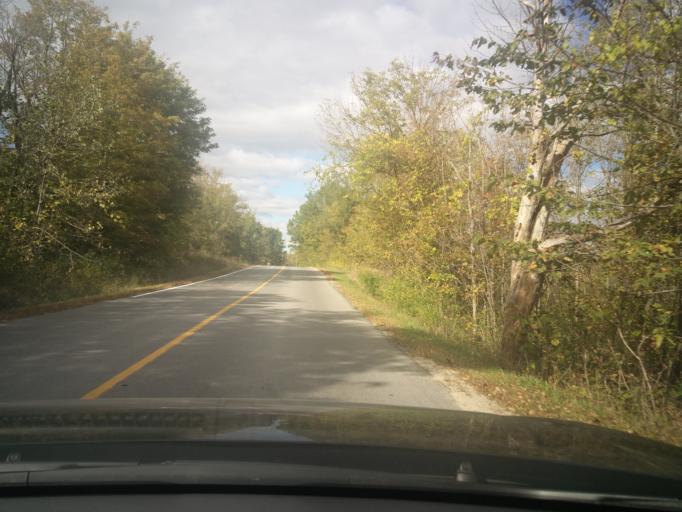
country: CA
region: Ontario
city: Perth
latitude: 44.6495
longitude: -76.5395
